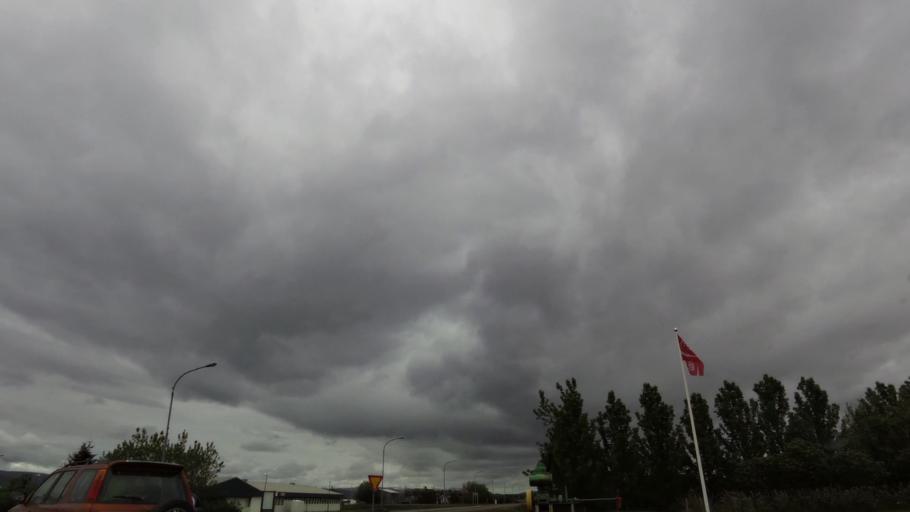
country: IS
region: West
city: Borgarnes
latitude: 65.1087
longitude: -21.7624
